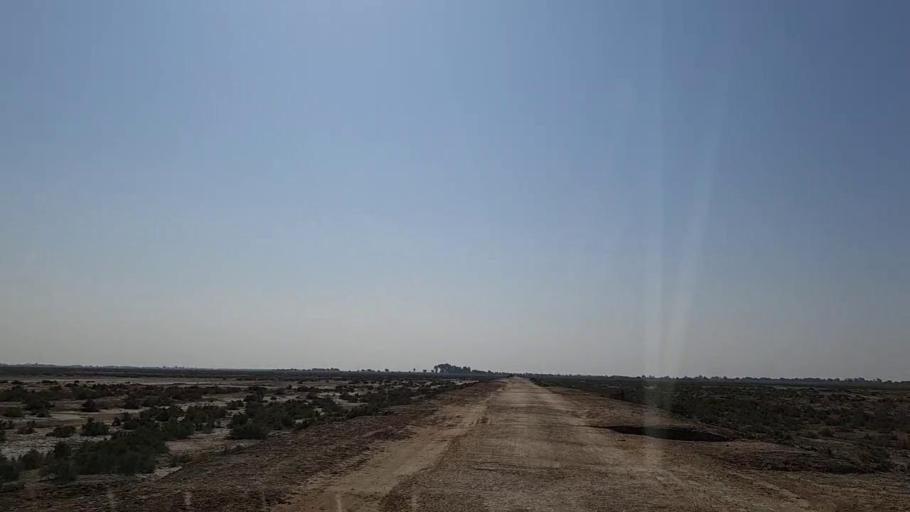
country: PK
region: Sindh
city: Chuhar Jamali
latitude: 24.5094
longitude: 68.0978
